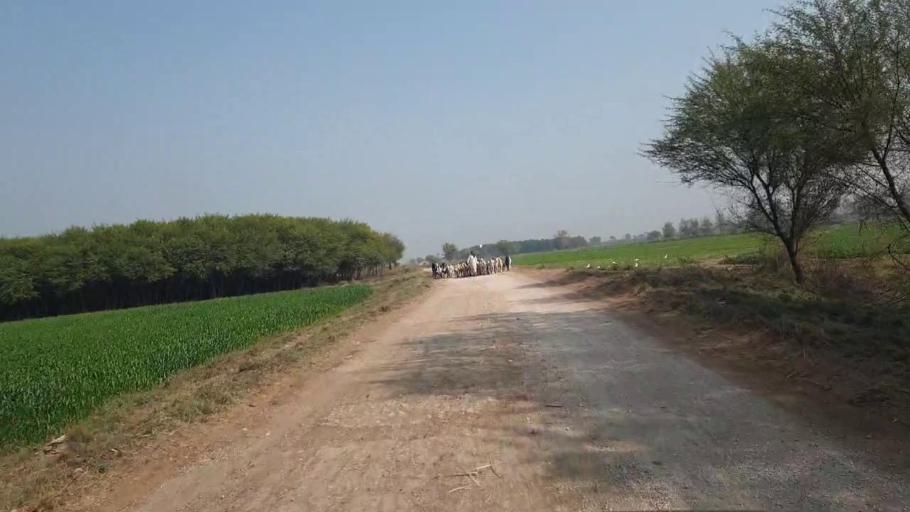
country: PK
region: Sindh
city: Hala
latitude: 25.9694
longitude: 68.4263
